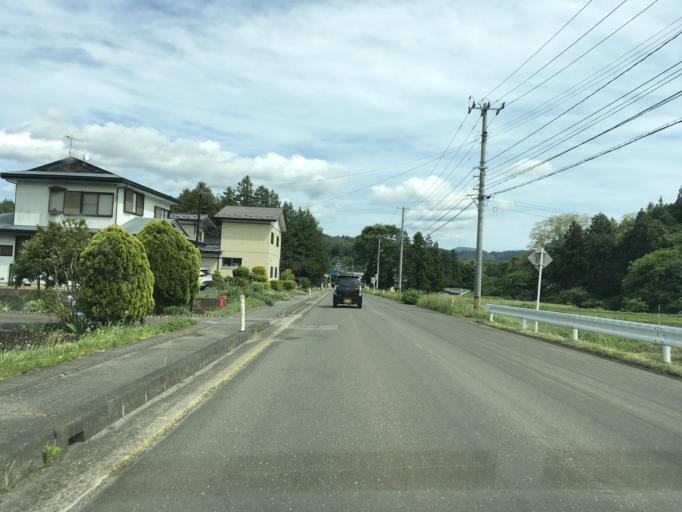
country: JP
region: Iwate
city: Mizusawa
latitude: 39.0573
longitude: 141.3623
